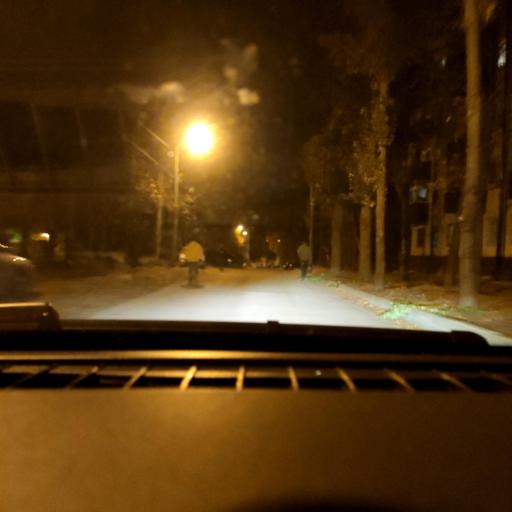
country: RU
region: Voronezj
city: Maslovka
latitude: 51.6191
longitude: 39.2427
